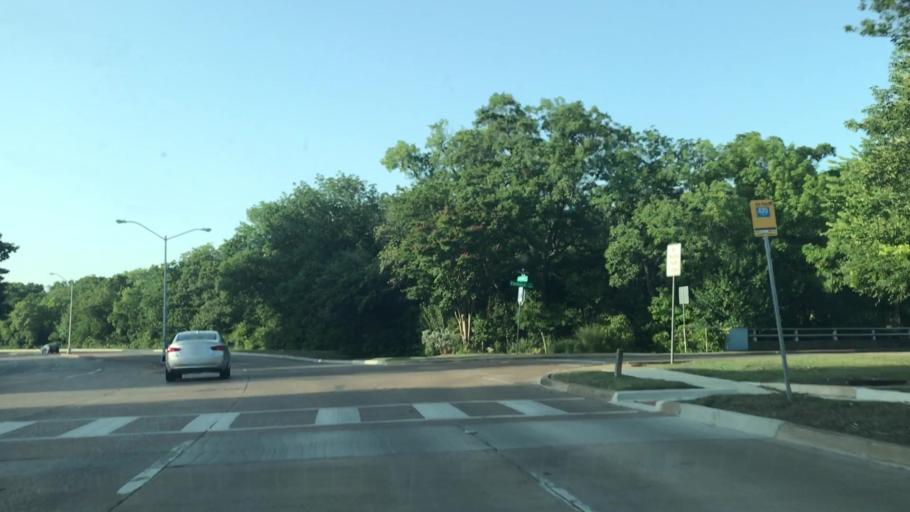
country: US
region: Texas
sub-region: Dallas County
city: Garland
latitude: 32.8575
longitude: -96.7008
